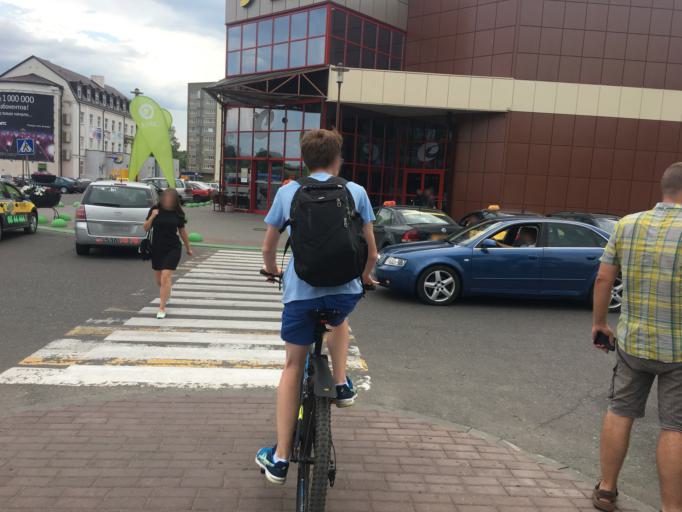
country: BY
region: Grodnenskaya
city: Hrodna
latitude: 53.6892
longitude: 23.8457
